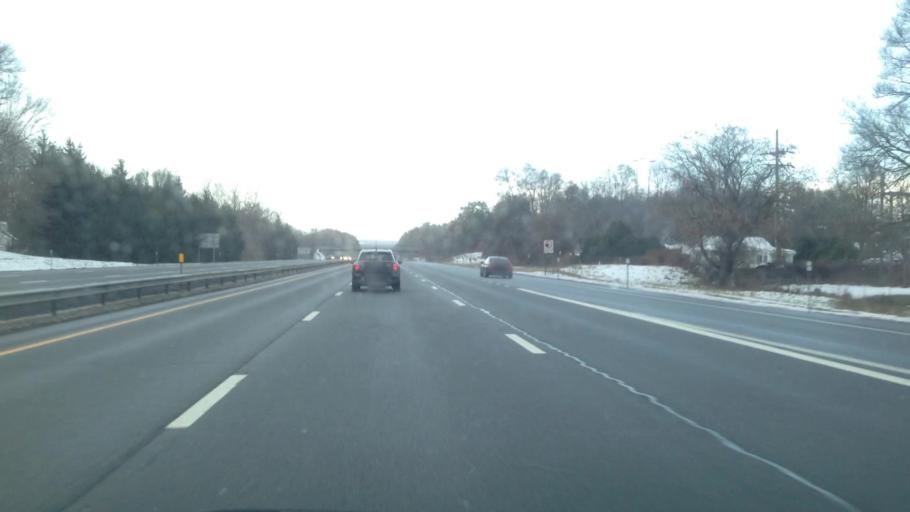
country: US
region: New York
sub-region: Schenectady County
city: Rotterdam
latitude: 42.7561
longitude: -73.9377
